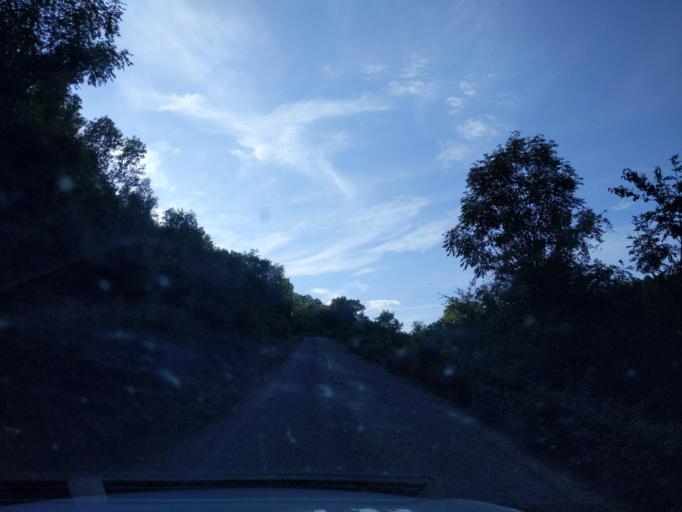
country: ES
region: La Rioja
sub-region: Provincia de La Rioja
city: Ojacastro
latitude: 42.3760
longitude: -3.0068
